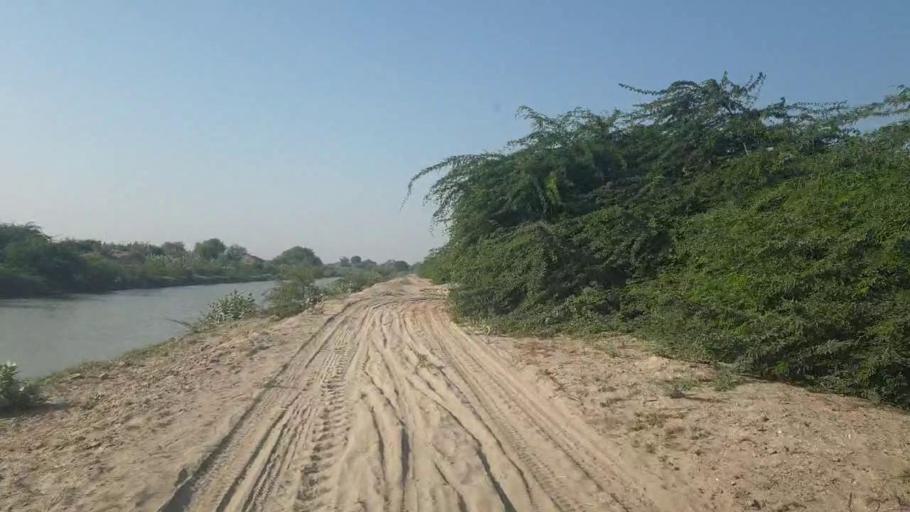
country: PK
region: Sindh
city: Tando Bago
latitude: 24.7223
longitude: 68.9197
